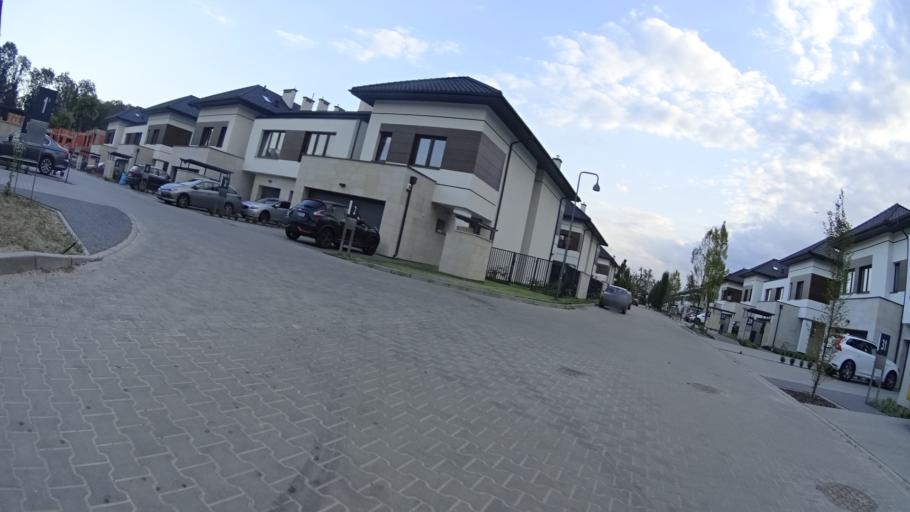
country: PL
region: Masovian Voivodeship
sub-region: Powiat warszawski zachodni
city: Ozarow Mazowiecki
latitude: 52.2332
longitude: 20.8063
